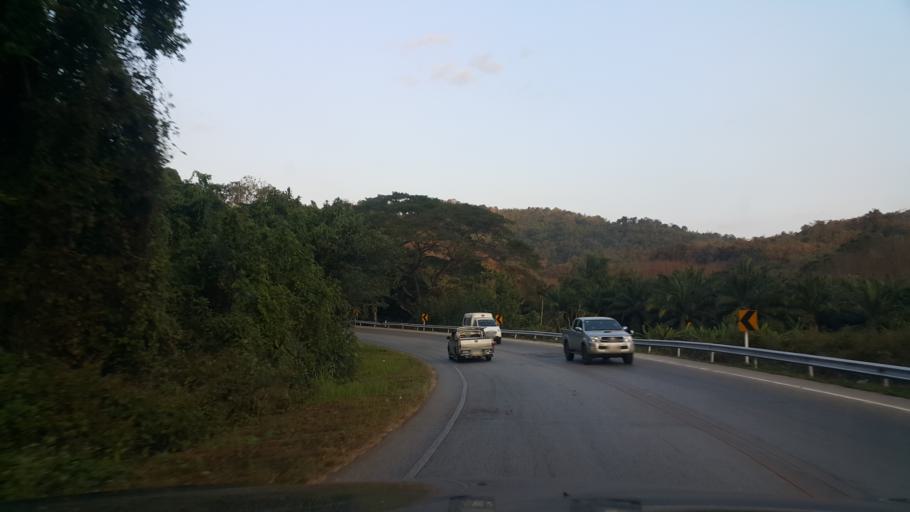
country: TH
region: Loei
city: Loei
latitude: 17.4665
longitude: 101.5939
